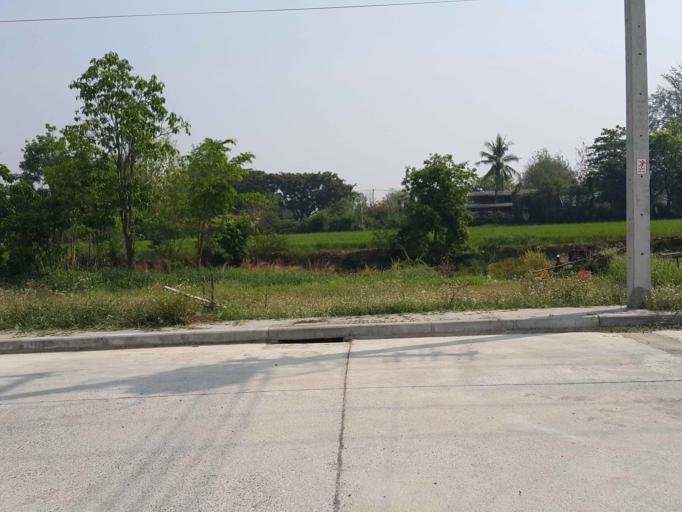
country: TH
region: Chiang Mai
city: San Kamphaeng
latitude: 18.7518
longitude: 99.0750
